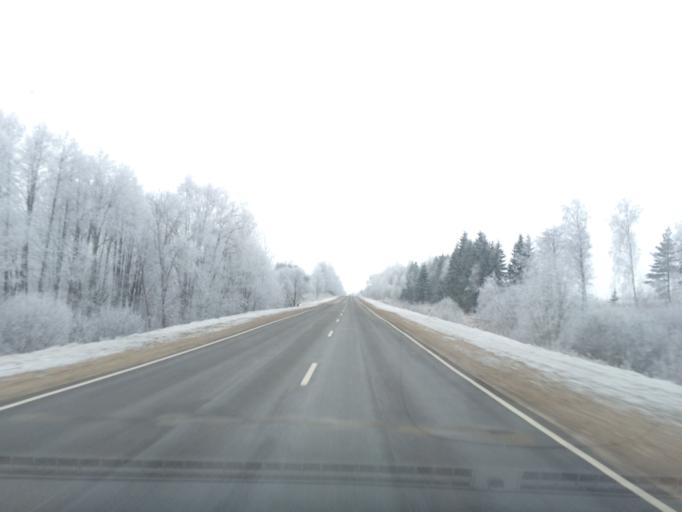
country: LV
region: Rezekne
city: Rezekne
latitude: 56.6399
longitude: 27.4800
